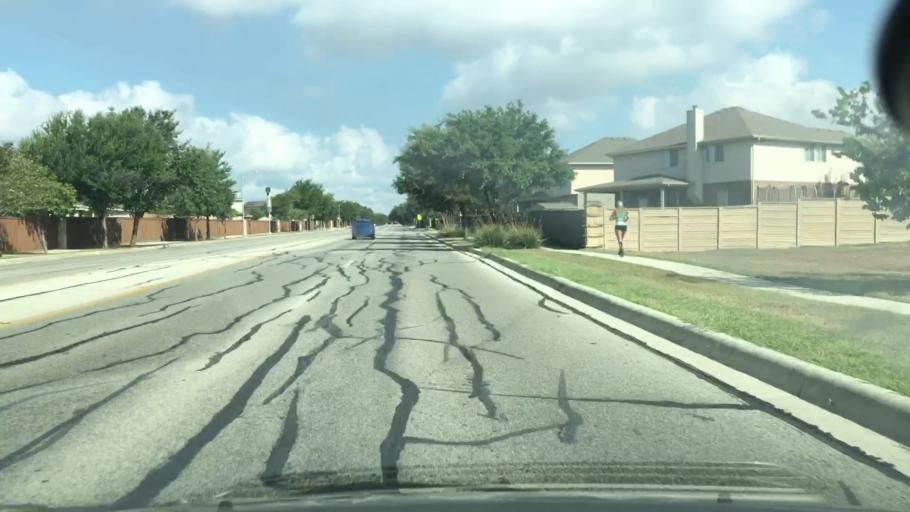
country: US
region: Texas
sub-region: Guadalupe County
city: Cibolo
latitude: 29.5742
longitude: -98.2419
